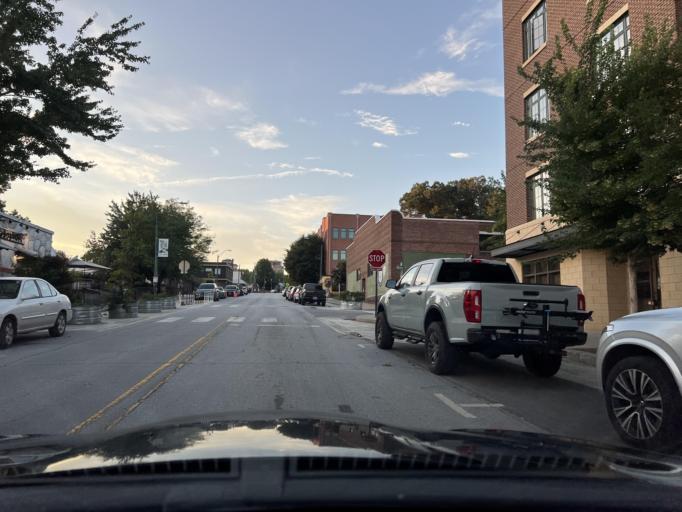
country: US
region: North Carolina
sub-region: Buncombe County
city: Asheville
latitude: 35.5890
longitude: -82.5547
